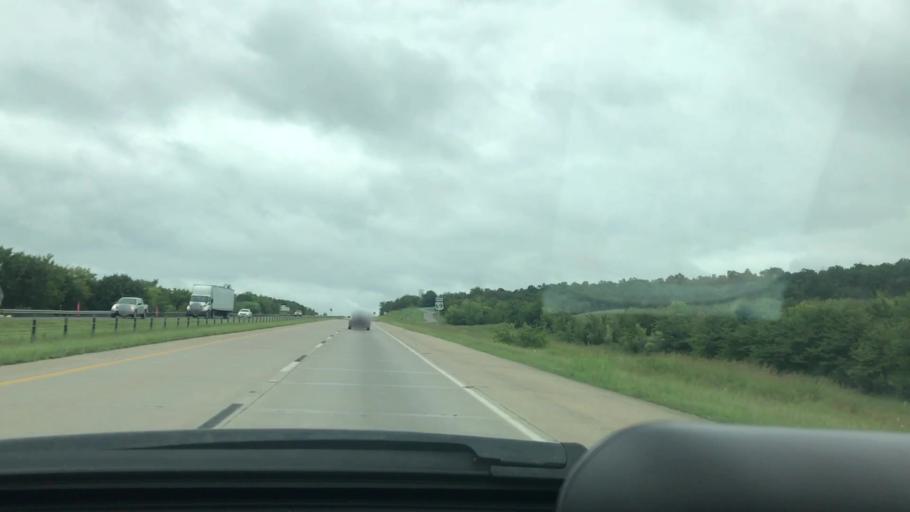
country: US
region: Oklahoma
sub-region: Pittsburg County
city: Krebs
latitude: 34.9634
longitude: -95.7244
